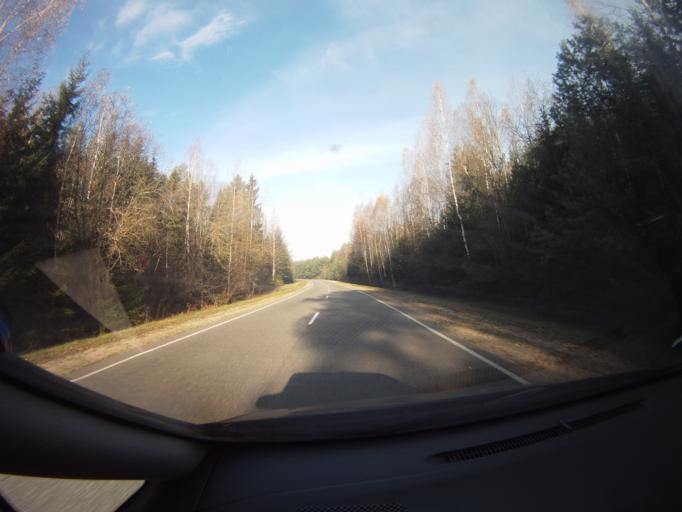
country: BY
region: Minsk
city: Il'ya
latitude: 54.4674
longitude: 27.2798
